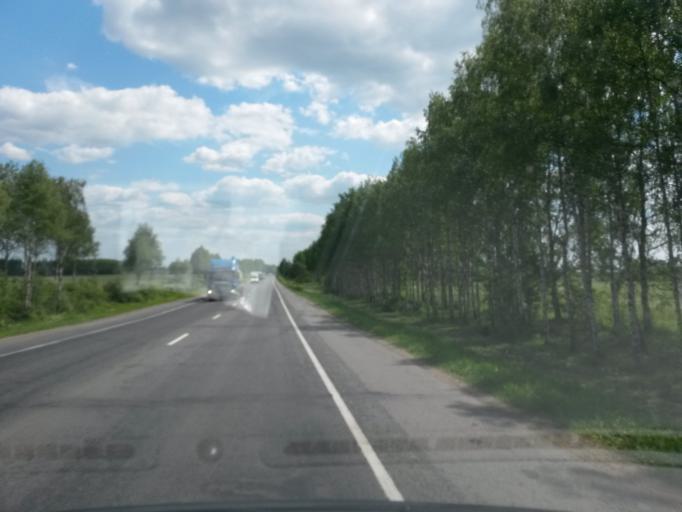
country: RU
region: Jaroslavl
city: Yaroslavl
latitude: 57.5573
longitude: 39.8642
